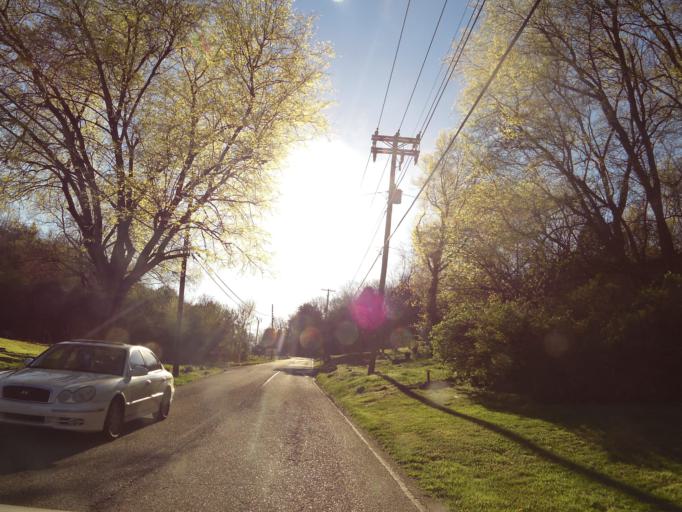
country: US
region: Tennessee
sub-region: Sevier County
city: Seymour
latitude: 35.9620
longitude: -83.8077
